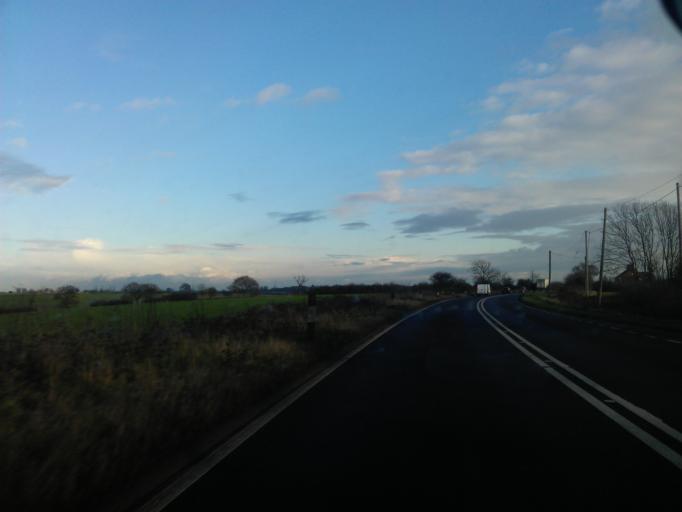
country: GB
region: England
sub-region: Suffolk
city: Shotley Gate
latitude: 51.9248
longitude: 1.1831
